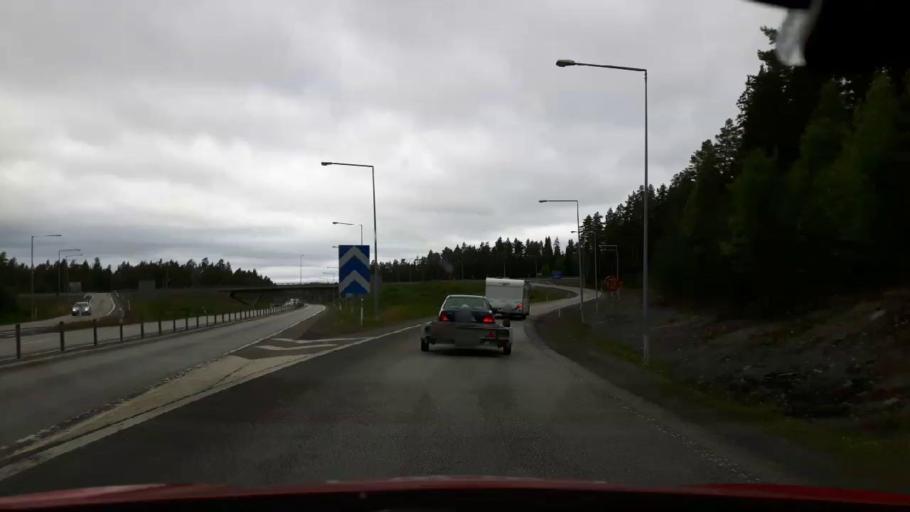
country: SE
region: Jaemtland
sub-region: OEstersunds Kommun
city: Ostersund
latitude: 63.2021
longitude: 14.6792
